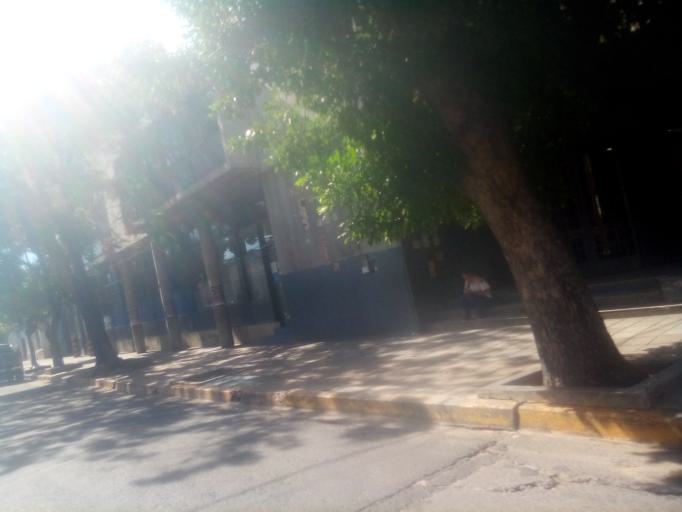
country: AR
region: Corrientes
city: Corrientes
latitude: -27.4697
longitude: -58.8371
